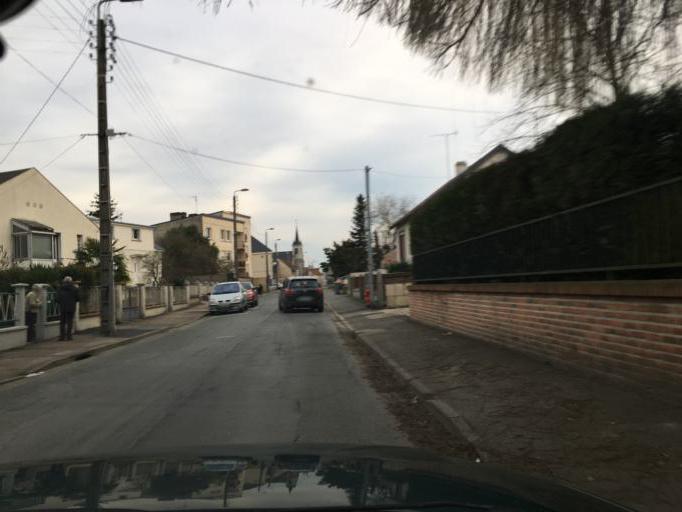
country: FR
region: Centre
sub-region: Departement du Loiret
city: Saran
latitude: 47.9350
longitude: 1.8931
